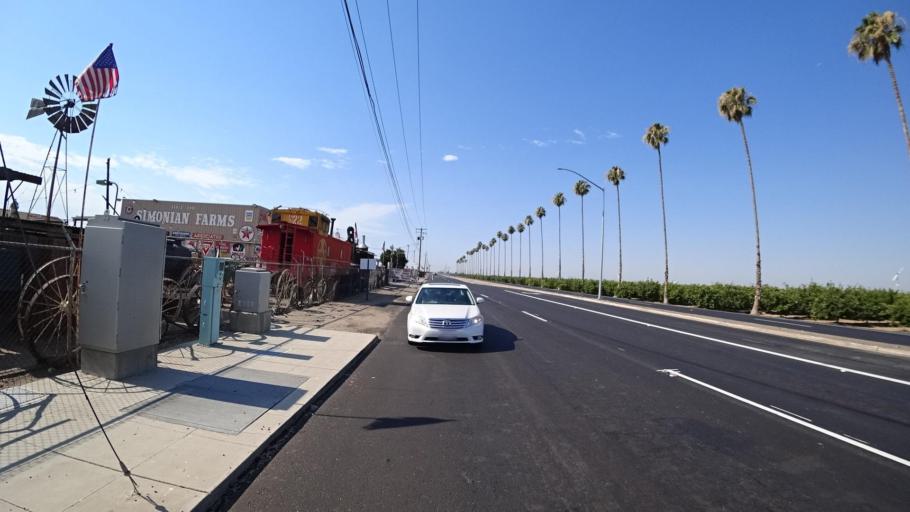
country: US
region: California
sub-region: Fresno County
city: Sunnyside
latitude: 36.7073
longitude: -119.6999
